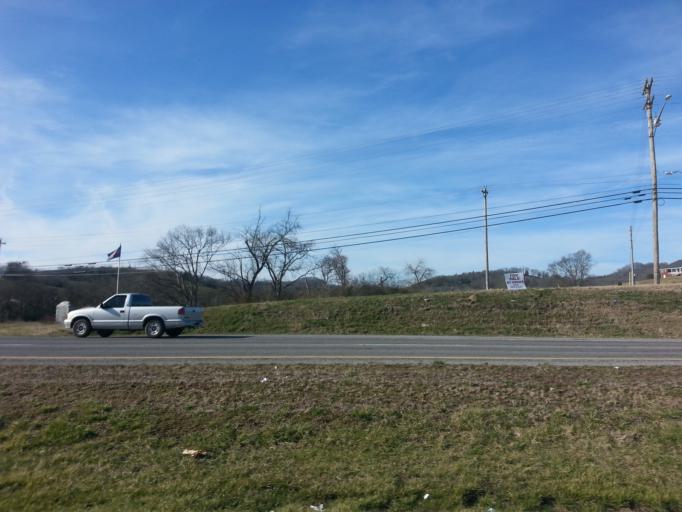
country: US
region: Tennessee
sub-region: Cannon County
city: Woodbury
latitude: 35.8254
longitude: -86.0857
